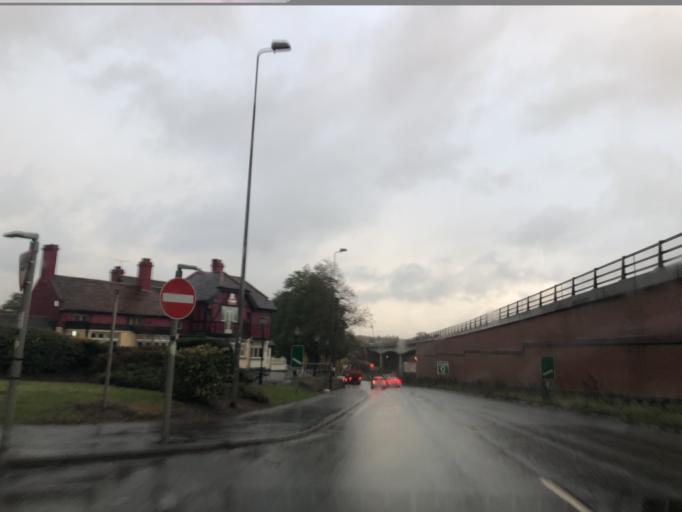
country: GB
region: England
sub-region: Solihull
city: Hampton in Arden
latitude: 52.4458
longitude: -1.6901
